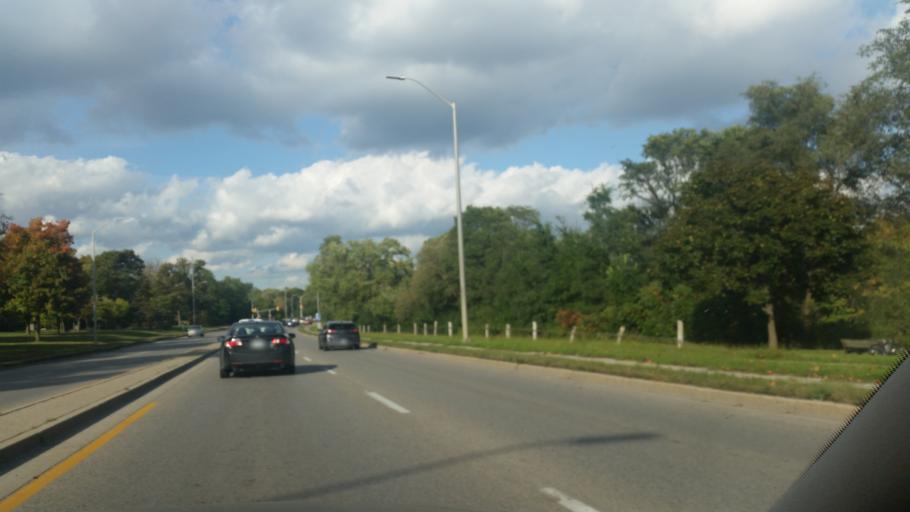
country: CA
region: Ontario
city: London
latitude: 42.9734
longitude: -81.2913
